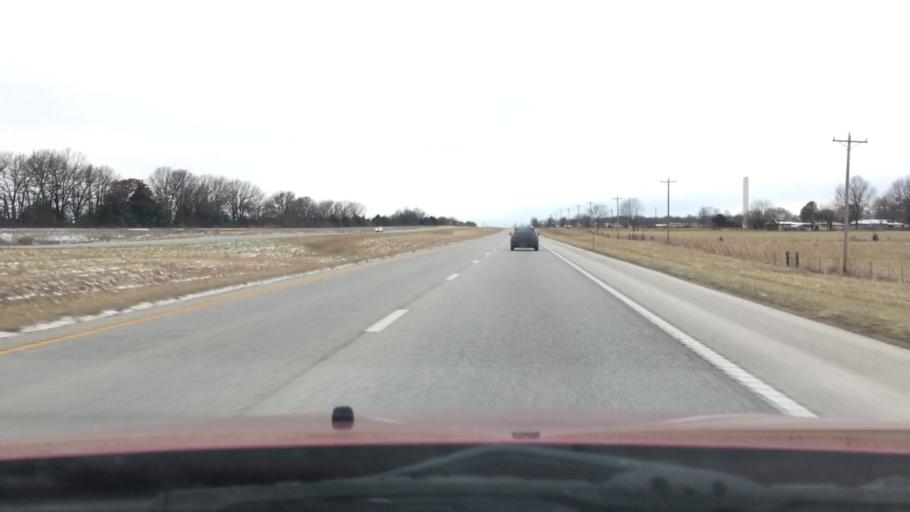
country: US
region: Missouri
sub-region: Webster County
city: Seymour
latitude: 37.1707
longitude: -92.8364
